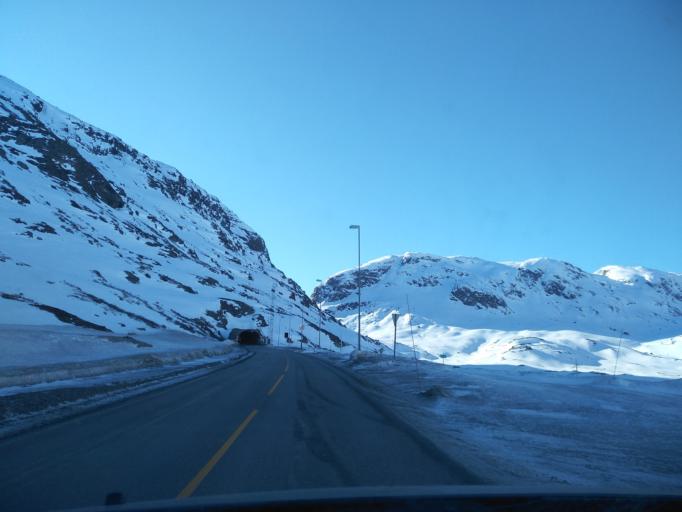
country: NO
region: Aust-Agder
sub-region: Bykle
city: Hovden
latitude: 59.8498
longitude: 7.0884
